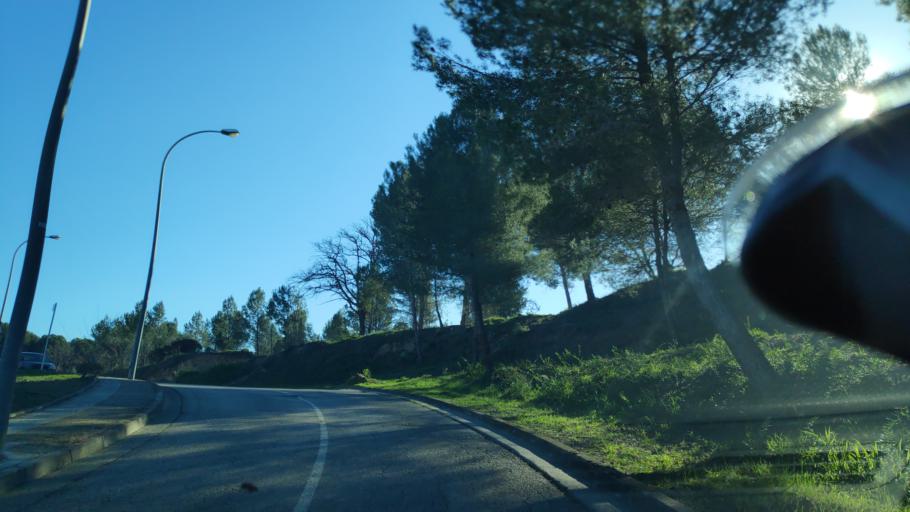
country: ES
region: Catalonia
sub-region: Provincia de Barcelona
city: Sant Quirze del Valles
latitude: 41.5232
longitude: 2.0701
